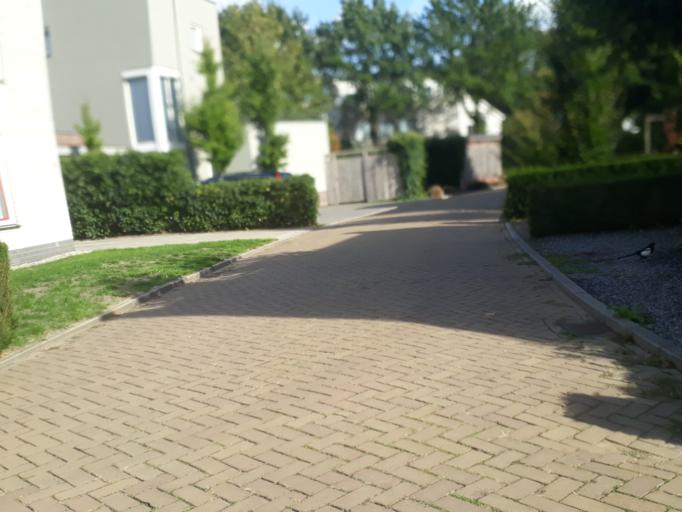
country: NL
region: Gelderland
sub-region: Gemeente Zevenaar
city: Zevenaar
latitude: 51.9415
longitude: 6.0567
